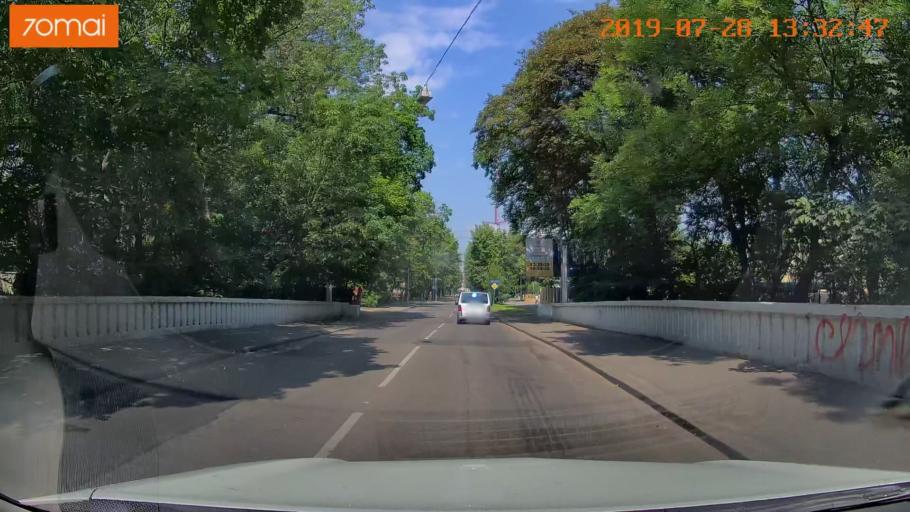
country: RU
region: Kaliningrad
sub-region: Gorod Kaliningrad
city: Kaliningrad
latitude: 54.7232
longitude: 20.4941
